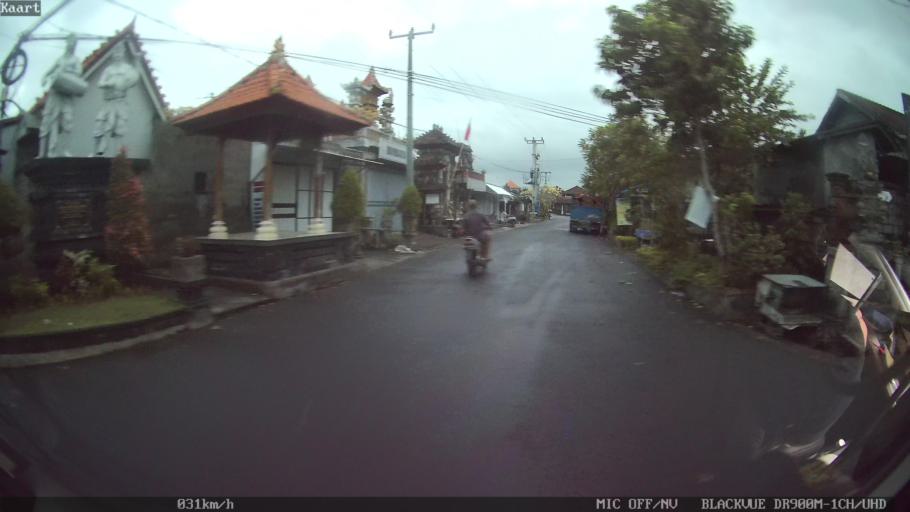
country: ID
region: Bali
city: Banjar Pasekan
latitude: -8.6166
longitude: 115.2751
